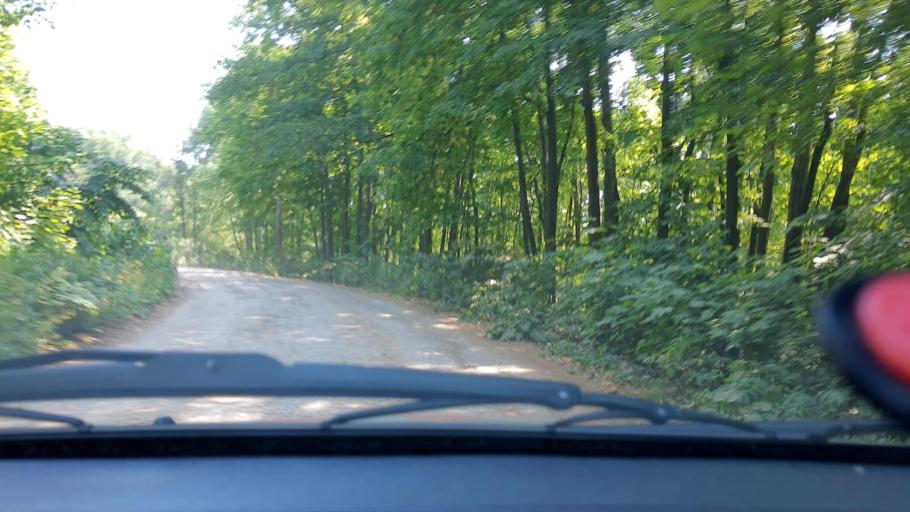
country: RU
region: Bashkortostan
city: Karmaskaly
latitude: 54.3873
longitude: 55.9024
